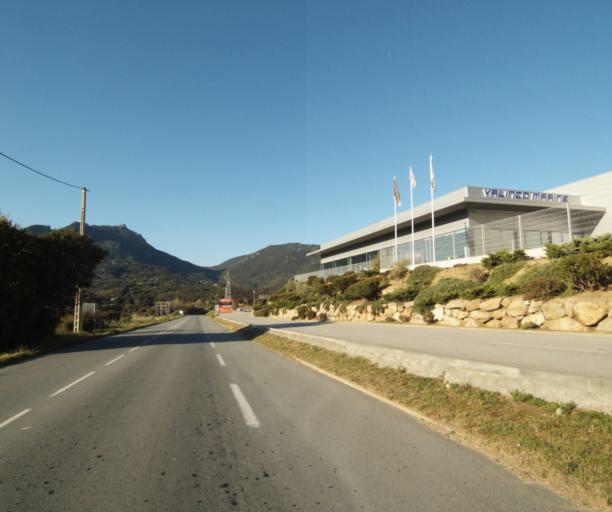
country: FR
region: Corsica
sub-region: Departement de la Corse-du-Sud
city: Propriano
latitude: 41.6638
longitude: 8.9187
